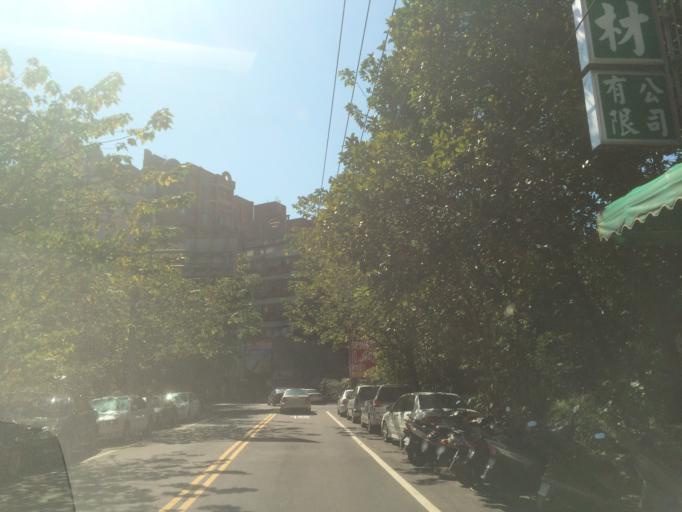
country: TW
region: Taiwan
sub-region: Hsinchu
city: Hsinchu
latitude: 24.7959
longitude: 120.9607
